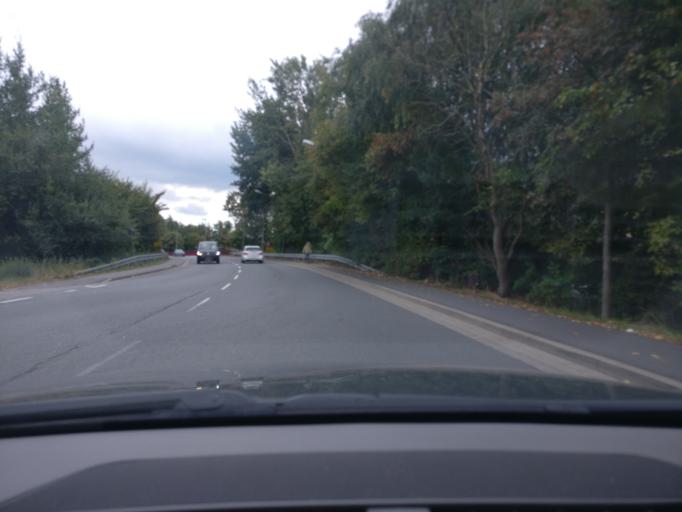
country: DE
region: Lower Saxony
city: Melle
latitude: 52.1948
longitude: 8.3422
